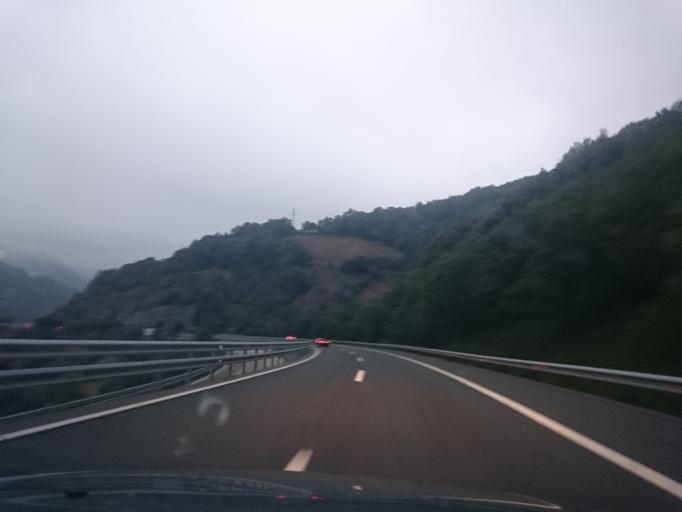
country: ES
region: Asturias
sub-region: Province of Asturias
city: Pola de Lena
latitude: 43.0538
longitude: -5.8200
